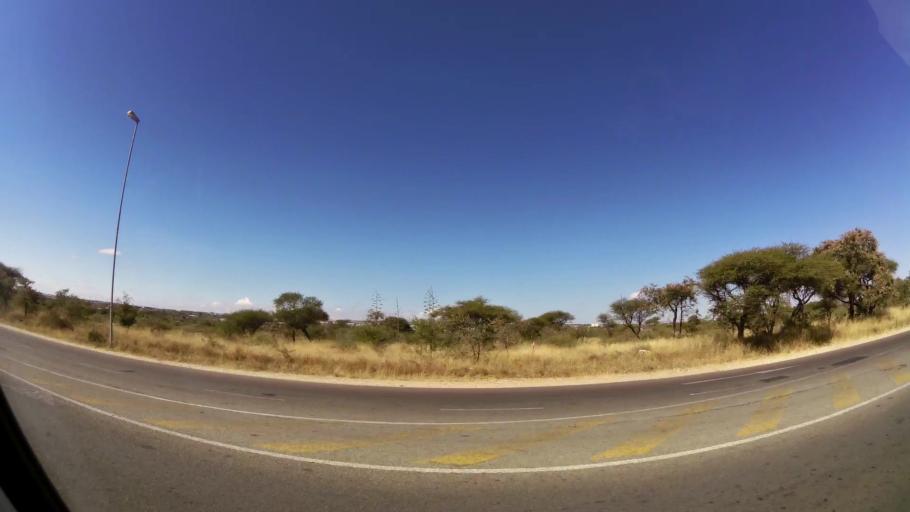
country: ZA
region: Limpopo
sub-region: Capricorn District Municipality
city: Polokwane
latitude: -23.8651
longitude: 29.4291
